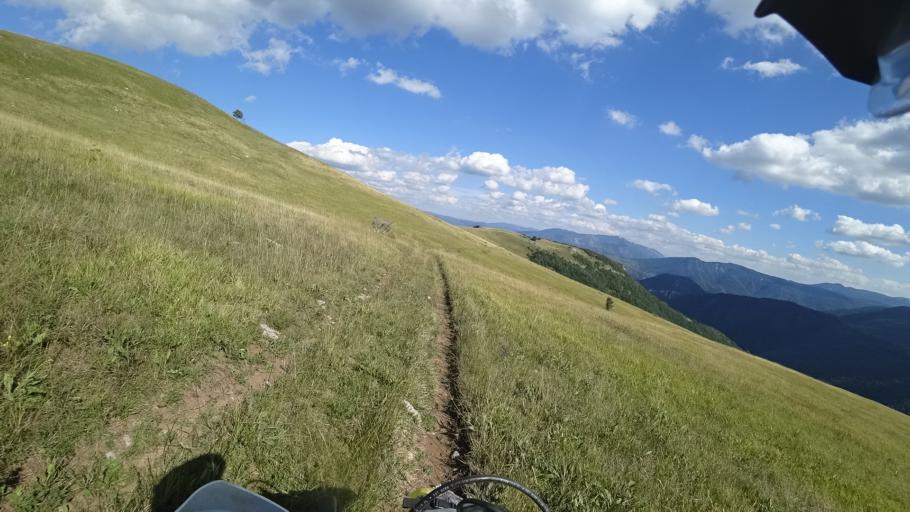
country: HR
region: Zadarska
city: Gracac
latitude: 44.3715
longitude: 16.0577
